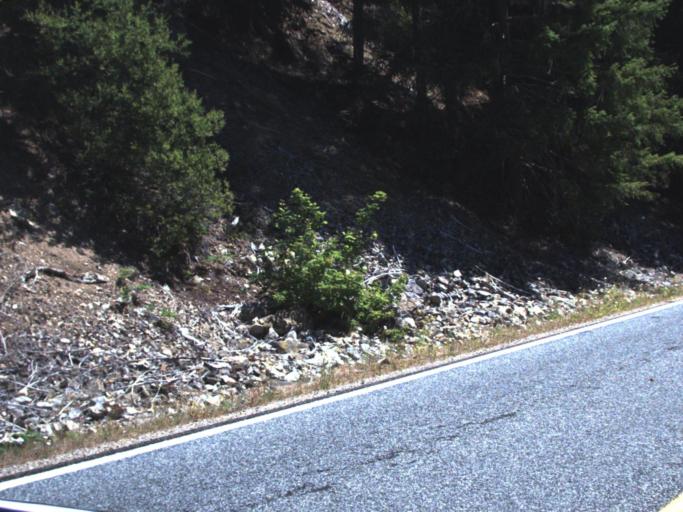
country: US
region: Washington
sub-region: King County
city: Enumclaw
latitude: 46.8061
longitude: -121.5548
